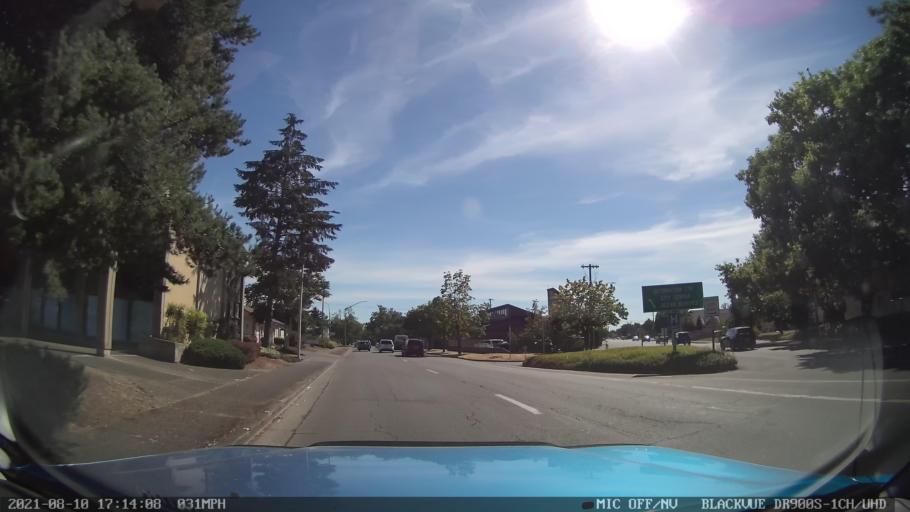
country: US
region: Oregon
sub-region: Marion County
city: Salem
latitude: 44.9555
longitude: -123.0220
